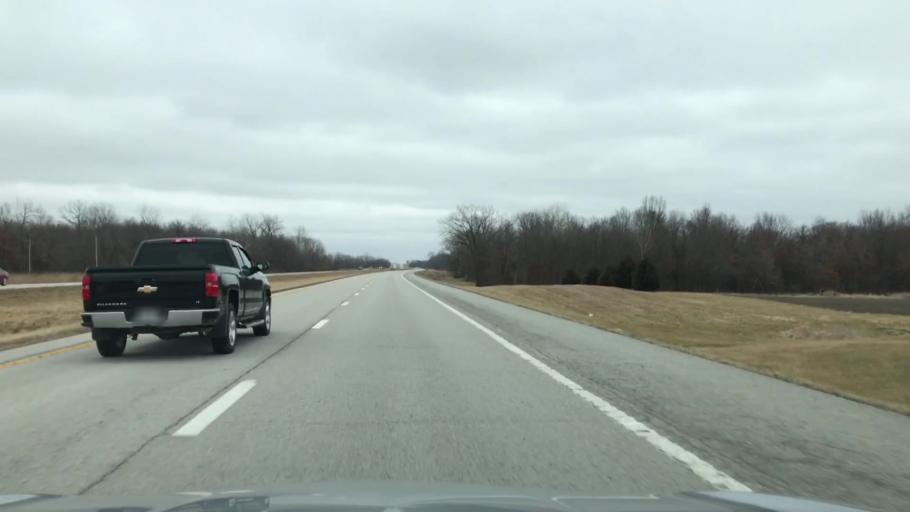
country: US
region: Missouri
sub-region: Livingston County
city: Chillicothe
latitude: 39.7767
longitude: -93.4412
